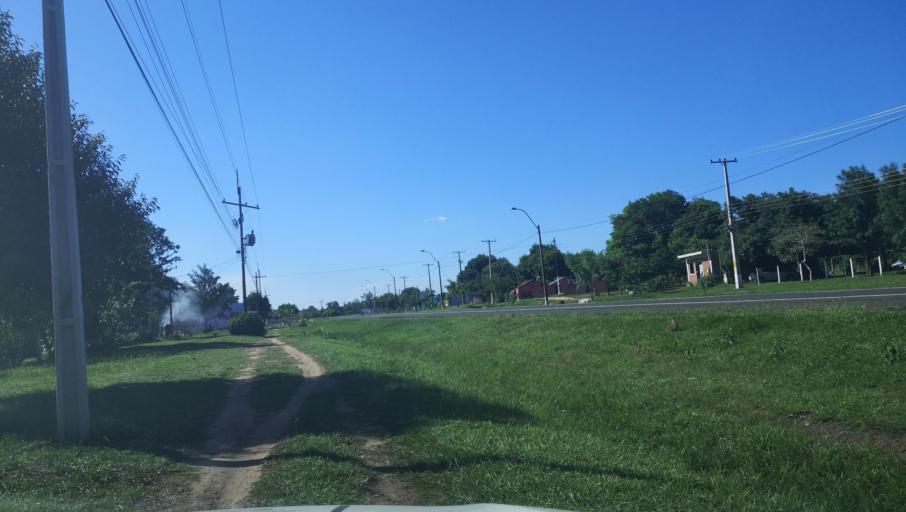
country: PY
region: Caaguazu
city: Carayao
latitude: -25.2059
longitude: -56.3991
